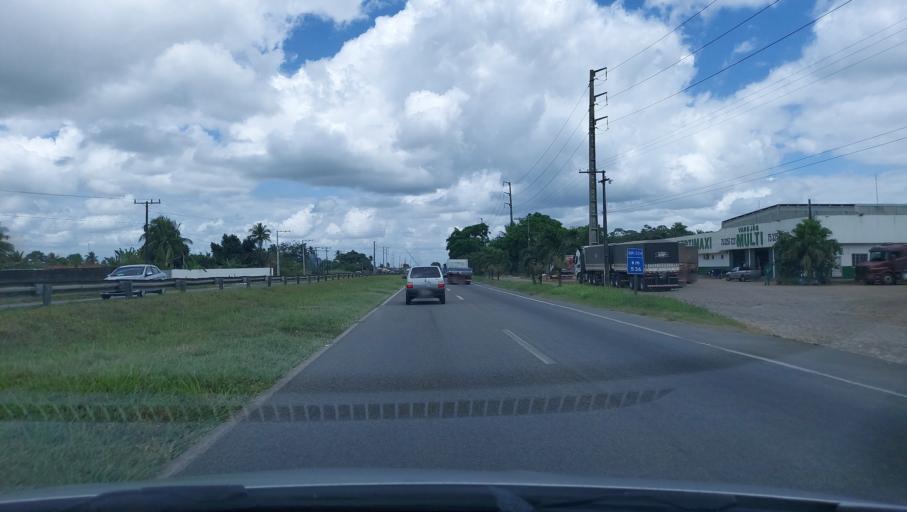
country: BR
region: Bahia
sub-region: Conceicao Do Jacuipe
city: Conceicao do Jacuipe
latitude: -12.3724
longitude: -38.8092
